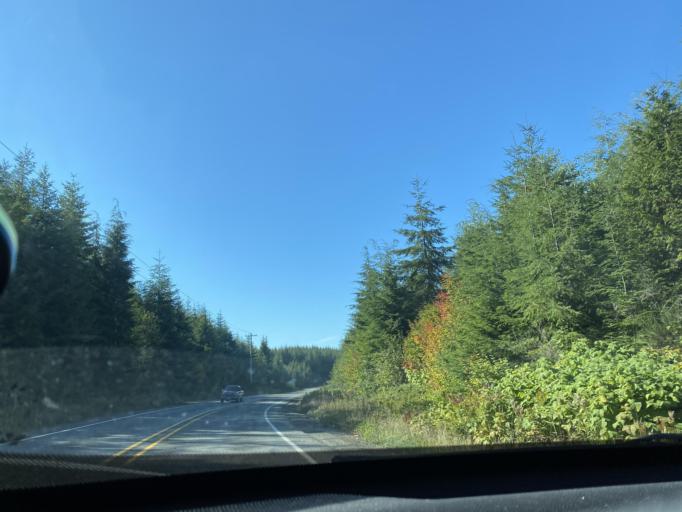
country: US
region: Washington
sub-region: Clallam County
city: Forks
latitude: 47.9573
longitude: -124.4481
